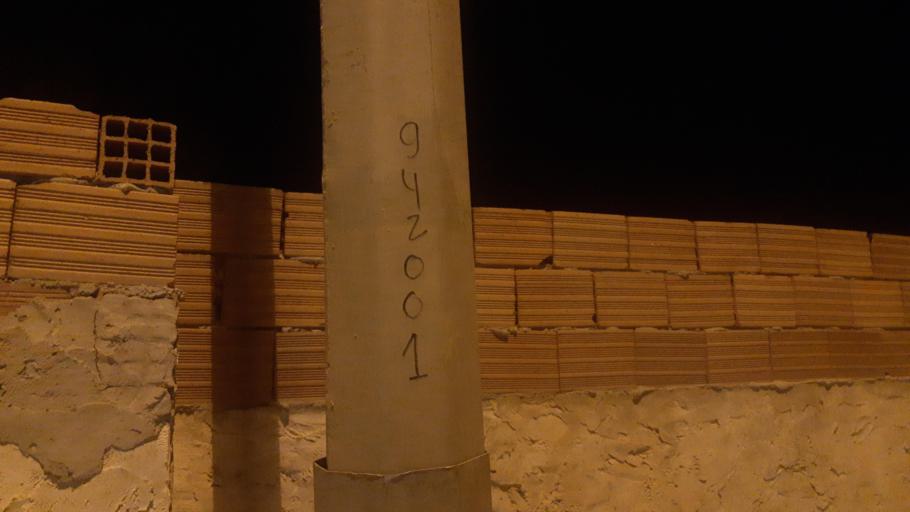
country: TN
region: Madanin
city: Midoun
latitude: 33.7787
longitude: 10.9394
